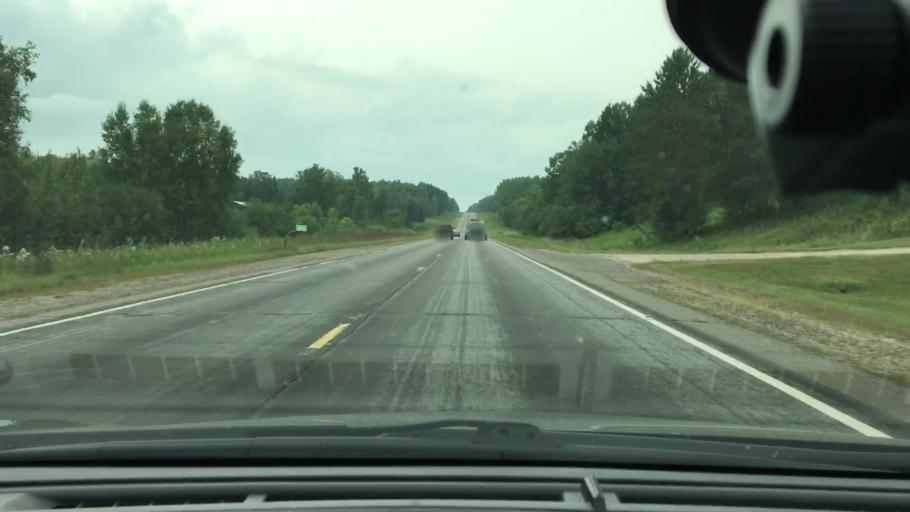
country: US
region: Minnesota
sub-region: Crow Wing County
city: Cross Lake
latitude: 46.6507
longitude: -93.9539
